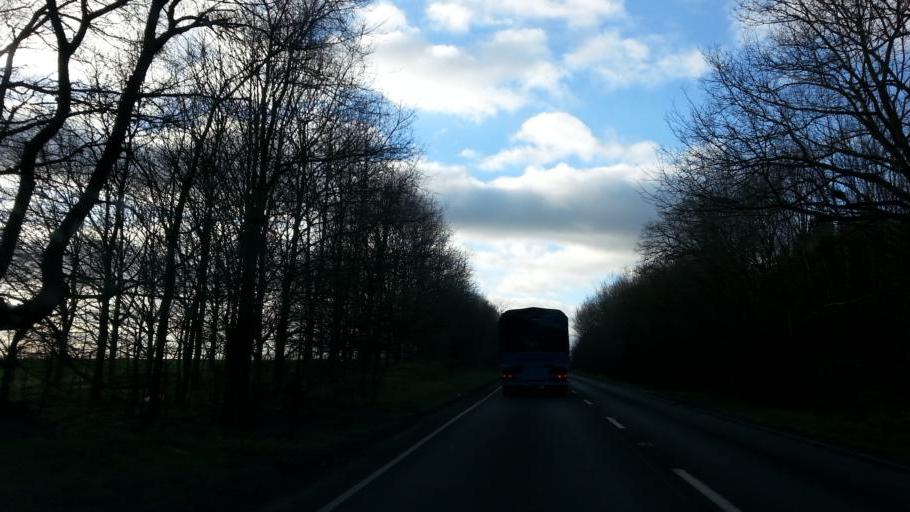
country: GB
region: England
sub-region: Norfolk
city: Harleston
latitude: 52.3664
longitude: 1.2258
